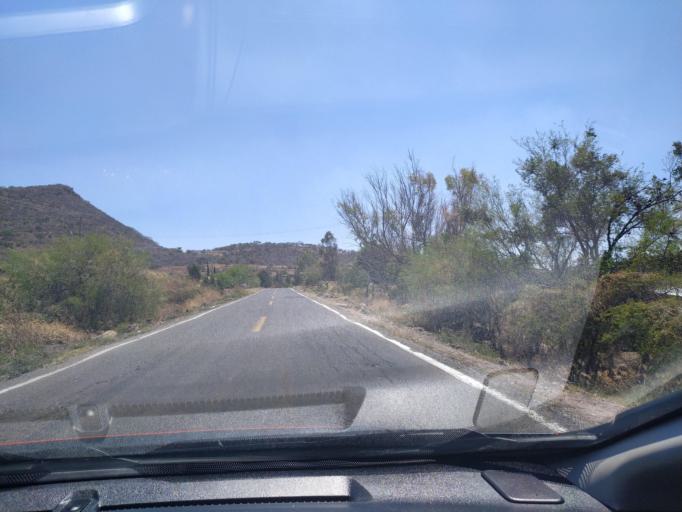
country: MX
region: Guanajuato
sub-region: San Francisco del Rincon
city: San Ignacio de Hidalgo
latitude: 20.8080
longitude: -101.8376
